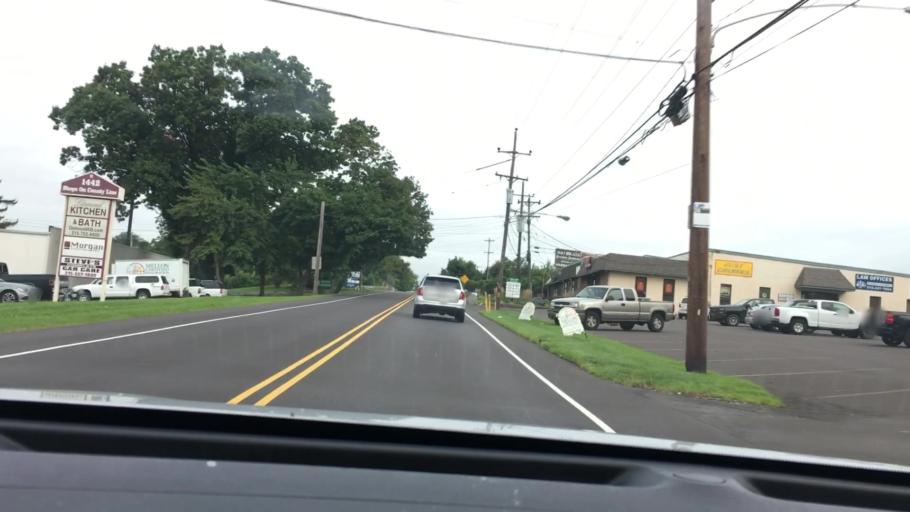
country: US
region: Pennsylvania
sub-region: Montgomery County
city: Bryn Athyn
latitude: 40.1622
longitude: -75.0558
